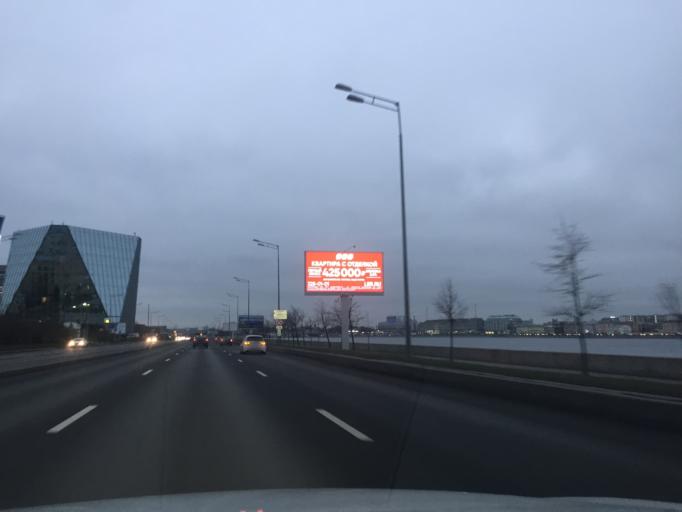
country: RU
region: St.-Petersburg
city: Centralniy
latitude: 59.9363
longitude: 30.4024
